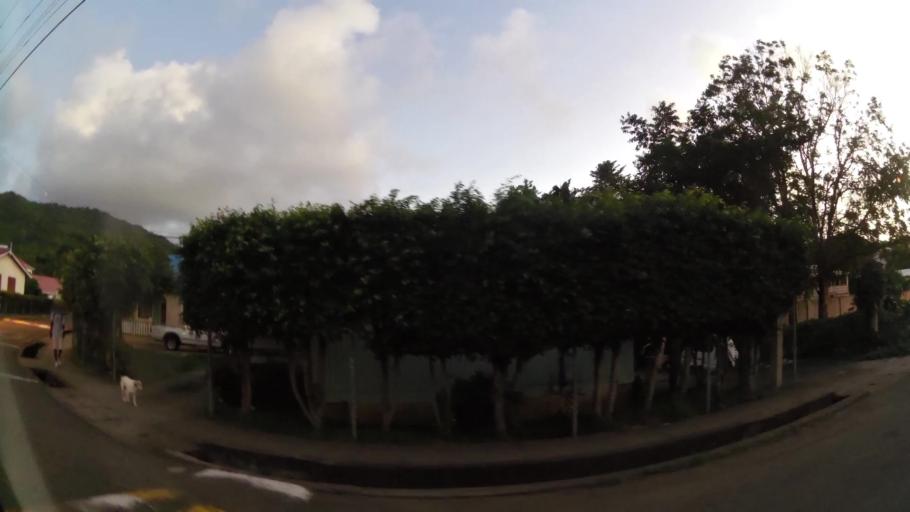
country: LC
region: Castries Quarter
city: Bisee
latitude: 14.0360
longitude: -60.9499
